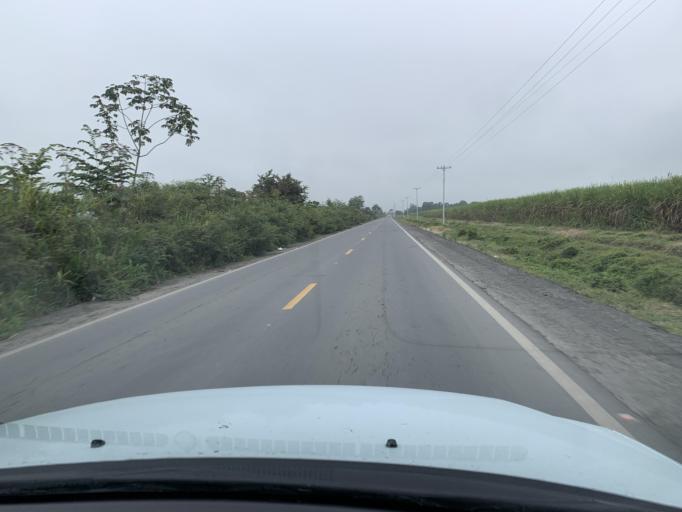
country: EC
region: Guayas
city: Coronel Marcelino Mariduena
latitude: -2.3280
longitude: -79.5239
